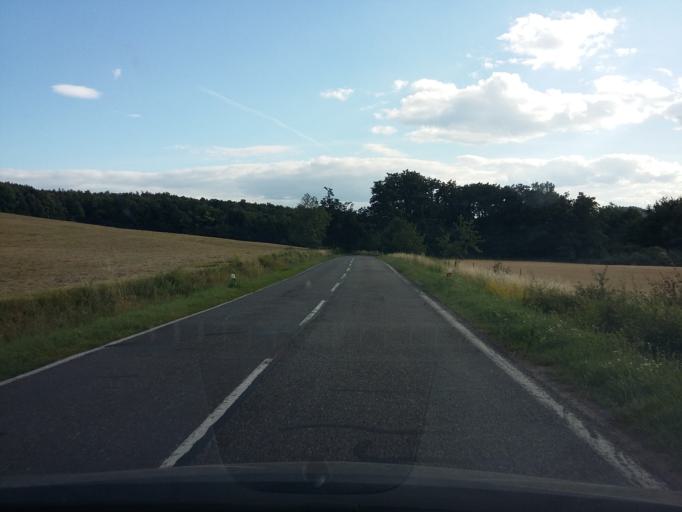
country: SK
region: Trnavsky
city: Smolenice
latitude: 48.5204
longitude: 17.3104
